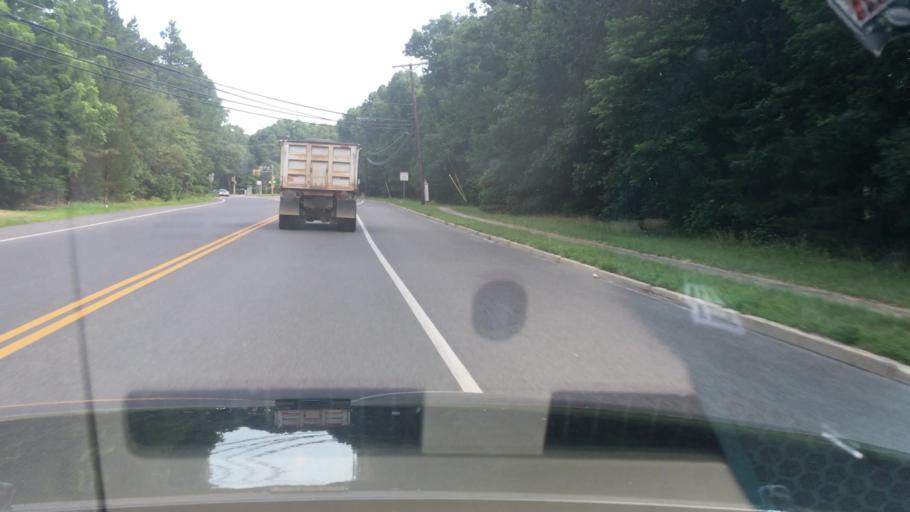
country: US
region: New Jersey
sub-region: Ocean County
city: Vista Center
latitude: 40.1483
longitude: -74.3980
